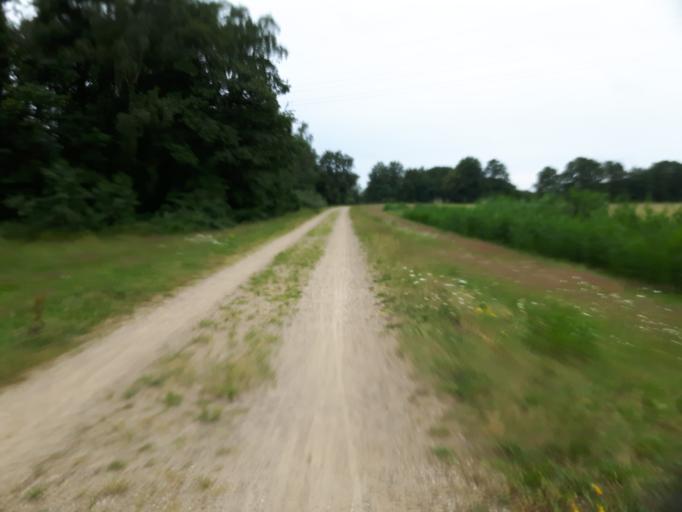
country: DE
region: Lower Saxony
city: Winsen
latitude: 53.3523
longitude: 10.1972
